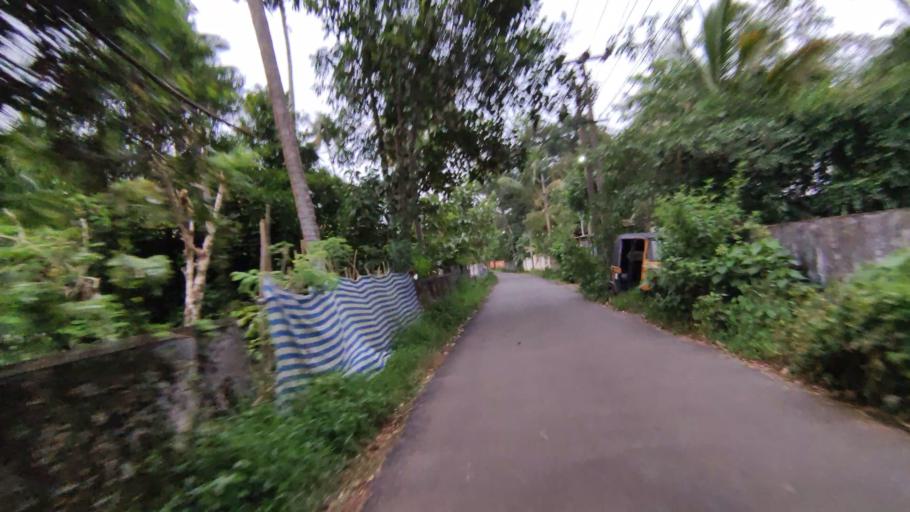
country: IN
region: Kerala
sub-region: Alappuzha
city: Shertallai
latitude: 9.6792
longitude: 76.3721
